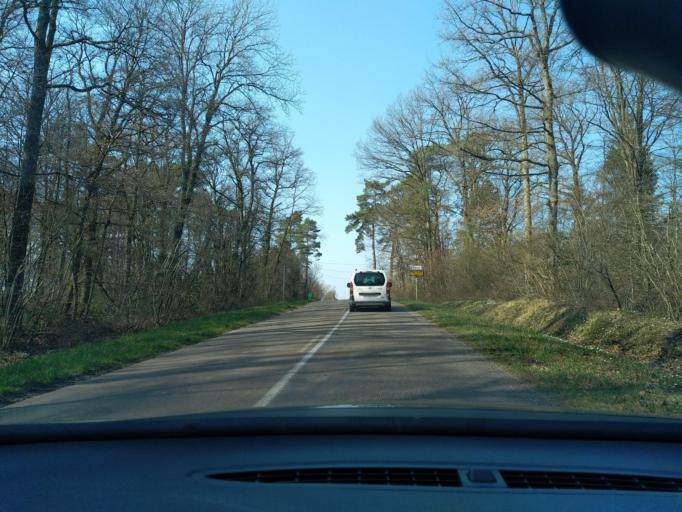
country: FR
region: Franche-Comte
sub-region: Departement du Jura
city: Dole
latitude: 47.0687
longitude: 5.5053
